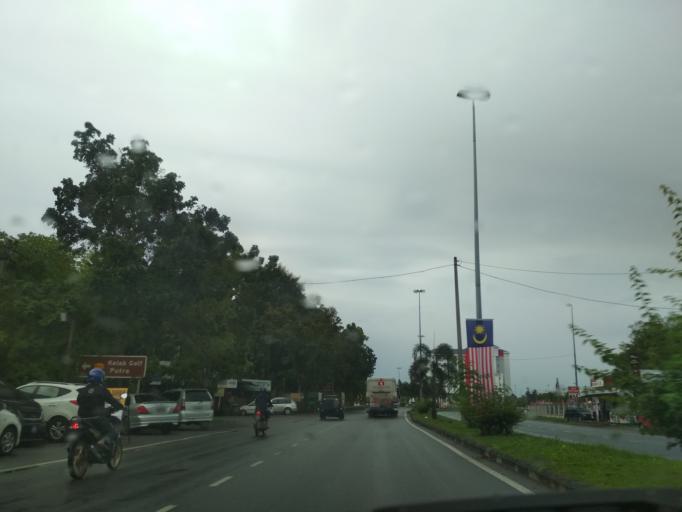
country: MY
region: Perlis
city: Kangar
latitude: 6.4293
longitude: 100.1851
